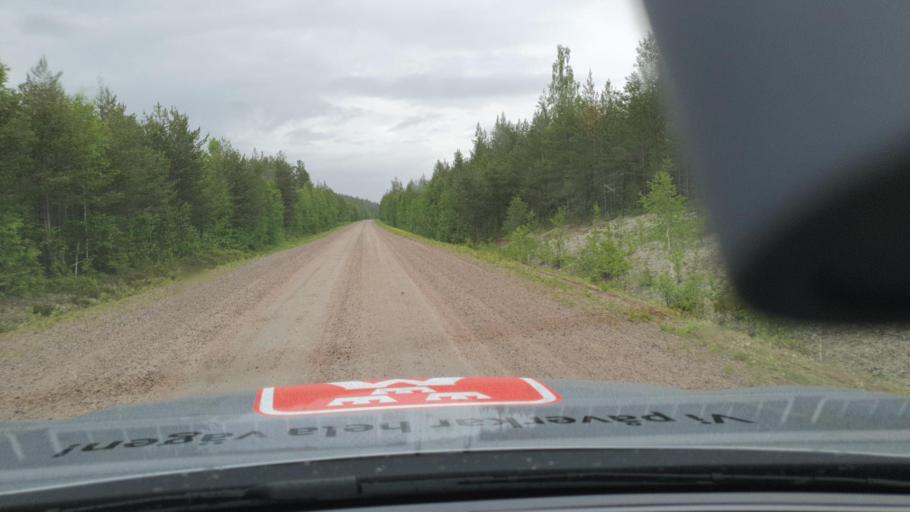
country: SE
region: Norrbotten
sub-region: Overkalix Kommun
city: OEverkalix
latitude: 66.5824
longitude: 22.7452
